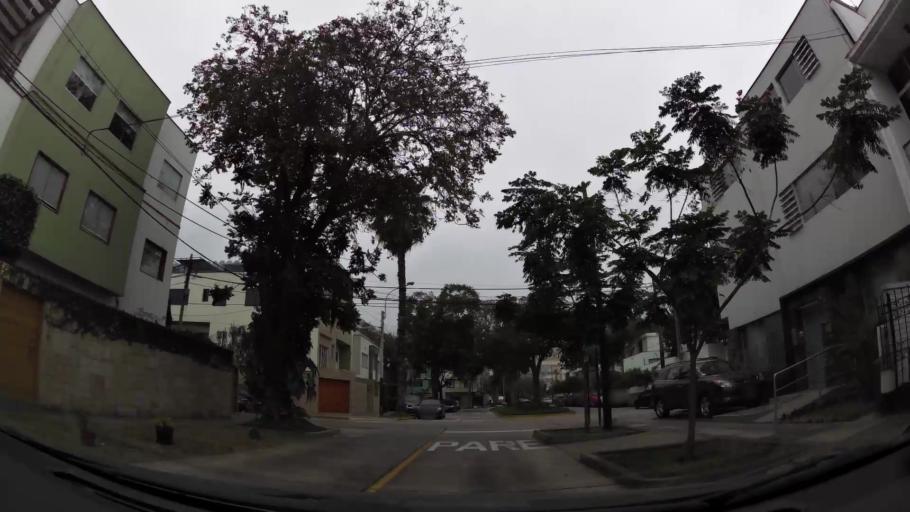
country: PE
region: Lima
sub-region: Lima
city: San Isidro
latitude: -12.0952
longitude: -77.0305
